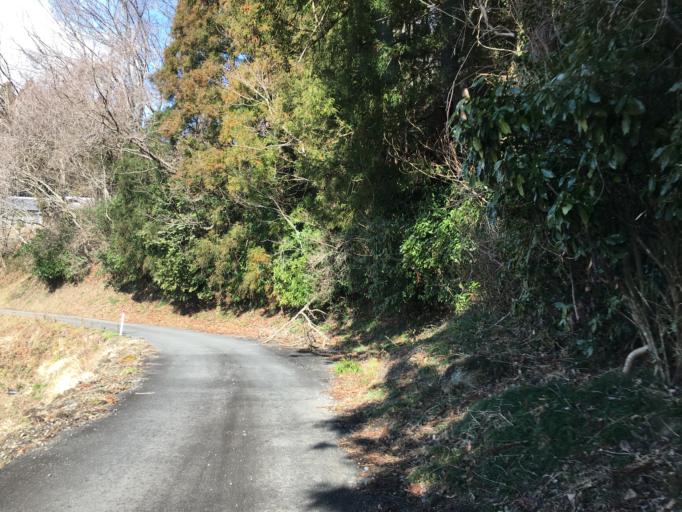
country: JP
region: Fukushima
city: Iwaki
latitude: 37.0053
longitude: 140.7966
